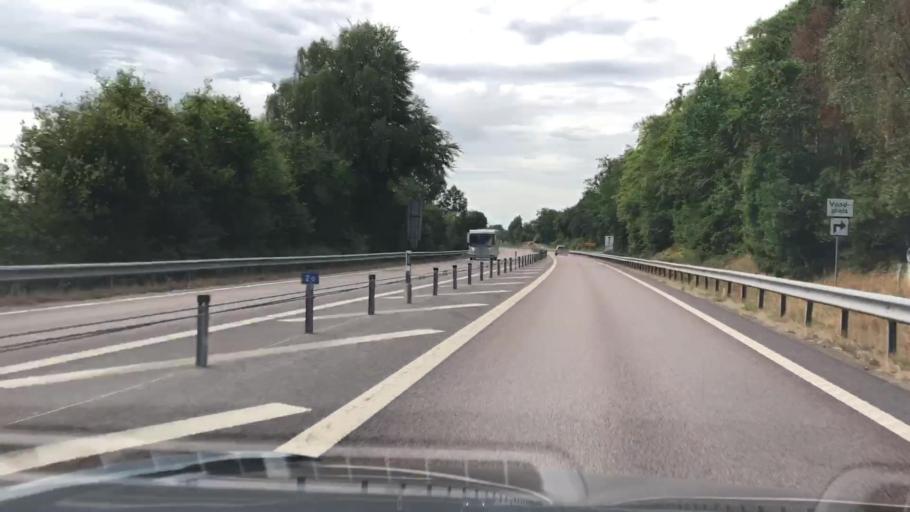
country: SE
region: Kalmar
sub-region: Torsas Kommun
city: Torsas
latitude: 56.3147
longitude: 16.0195
